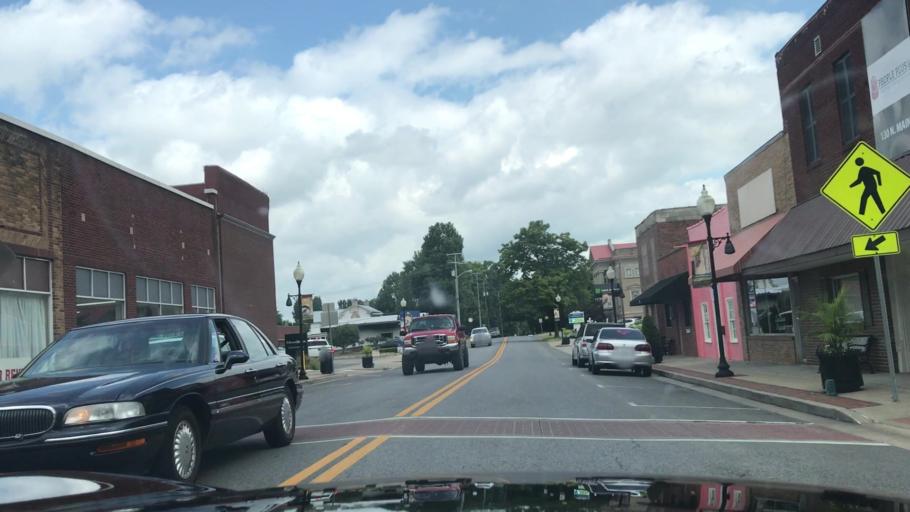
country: US
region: Kentucky
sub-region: Muhlenberg County
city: Greenville
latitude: 37.2018
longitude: -87.1786
